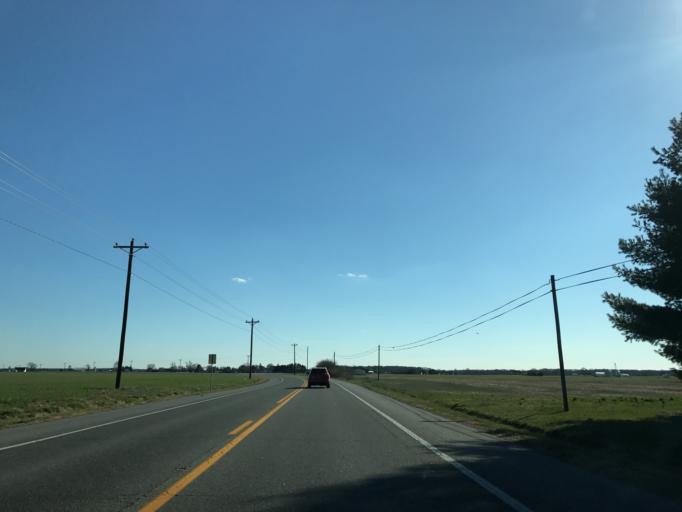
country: US
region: Maryland
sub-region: Caroline County
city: Greensboro
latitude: 39.1042
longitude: -75.8736
